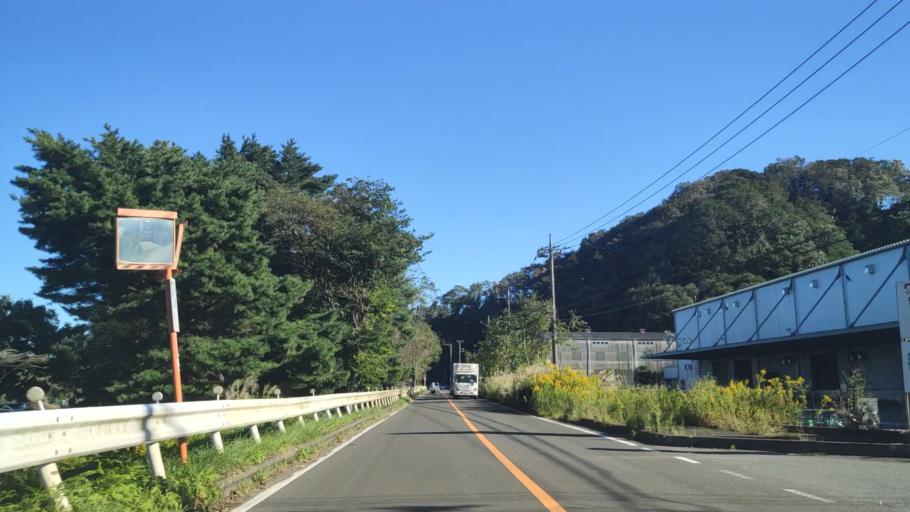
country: JP
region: Kanagawa
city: Zama
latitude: 35.5322
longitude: 139.3415
